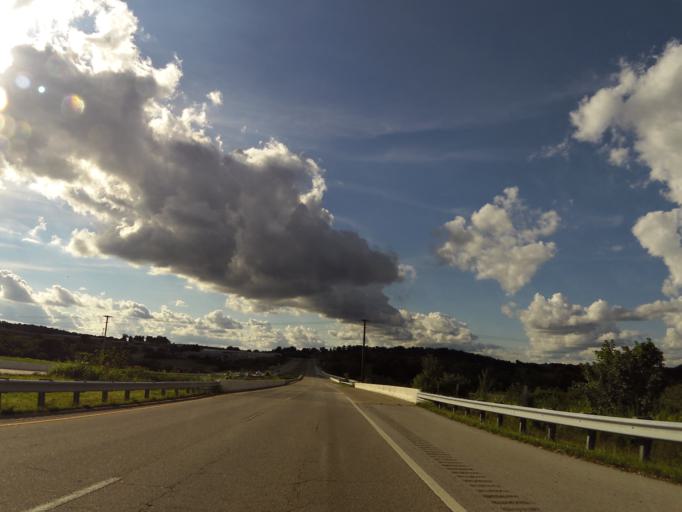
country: US
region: Tennessee
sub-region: Blount County
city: Alcoa
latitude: 35.8264
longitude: -83.9573
